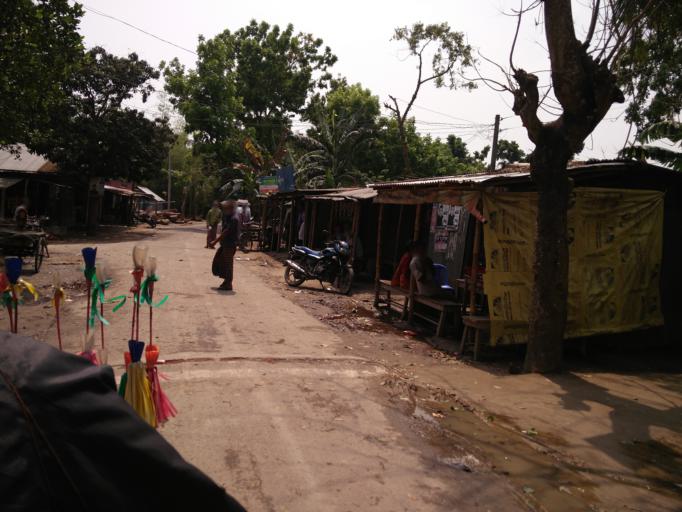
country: BD
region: Dhaka
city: Sherpur
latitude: 24.9357
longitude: 90.1588
